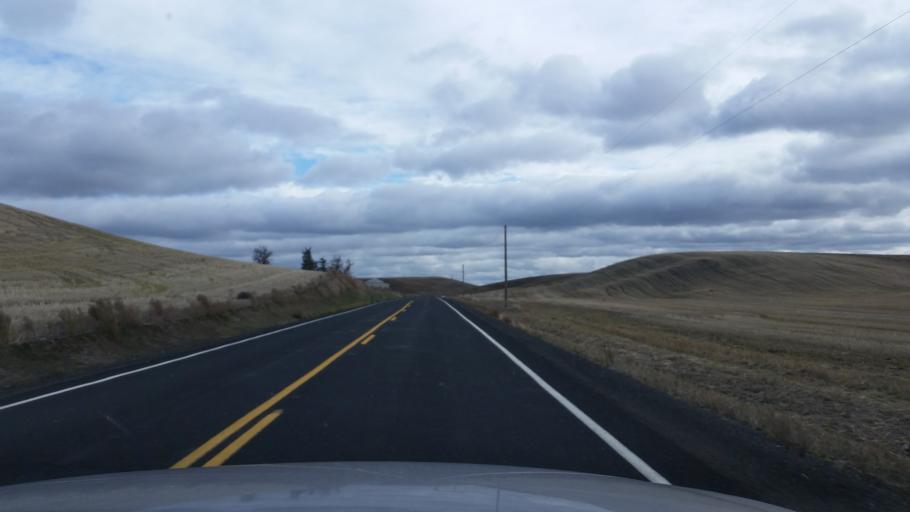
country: US
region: Washington
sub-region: Lincoln County
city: Davenport
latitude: 47.3513
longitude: -118.0286
